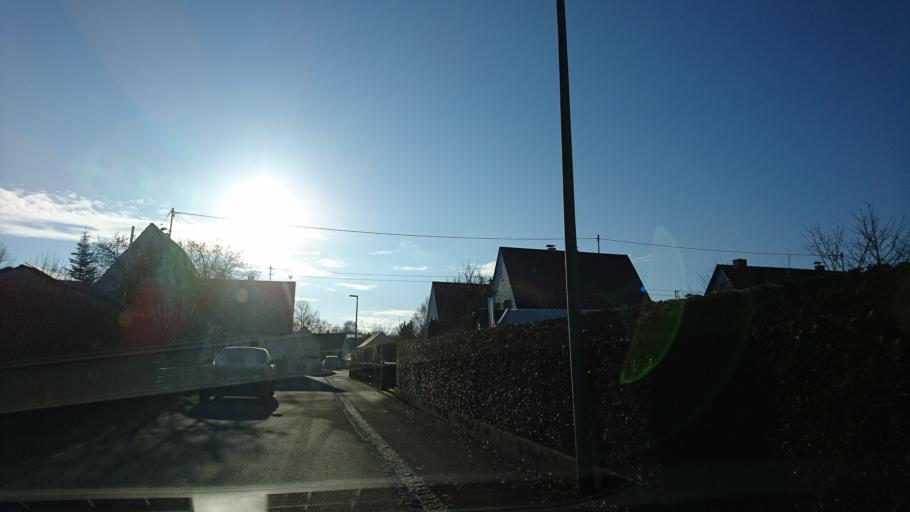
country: DE
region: Bavaria
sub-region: Swabia
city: Nordendorf
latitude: 48.5964
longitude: 10.8362
